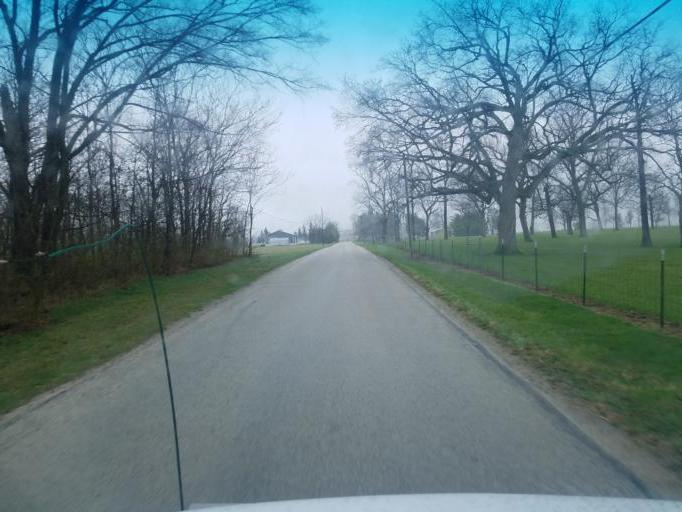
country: US
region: Ohio
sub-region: Wood County
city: North Baltimore
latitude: 41.2431
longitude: -83.6308
